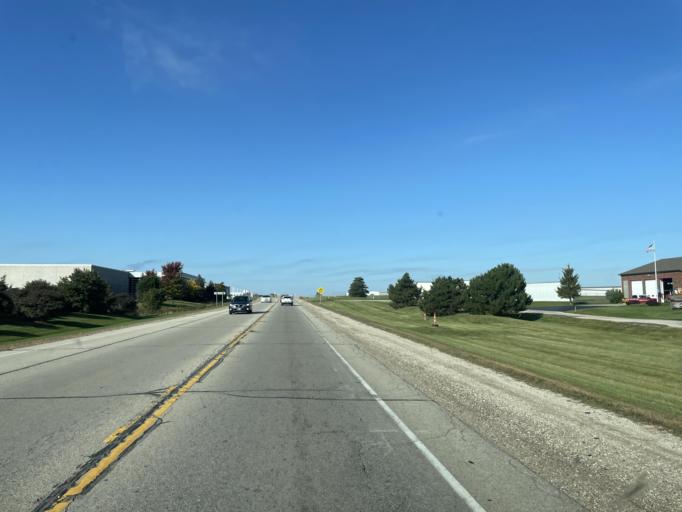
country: US
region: Wisconsin
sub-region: Kenosha County
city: Pleasant Prairie
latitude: 42.5894
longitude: -87.9249
